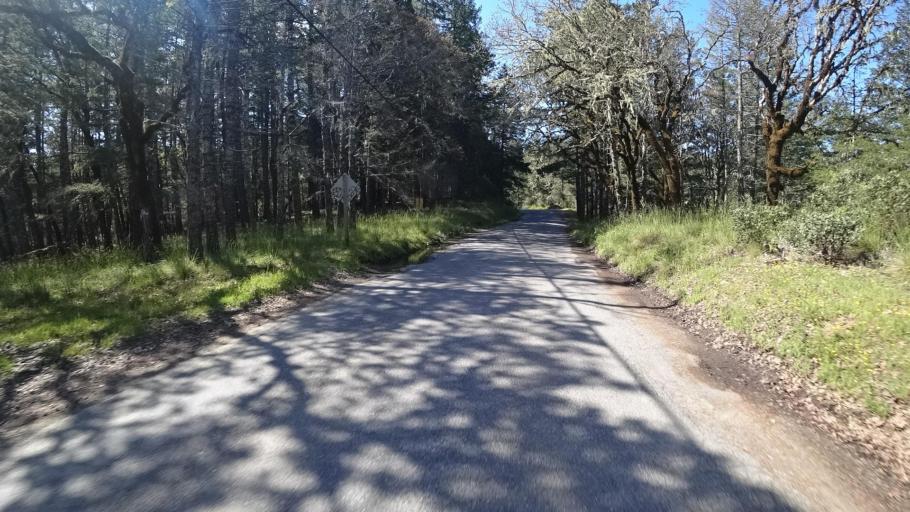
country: US
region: California
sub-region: Humboldt County
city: Redway
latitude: 40.0479
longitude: -123.6420
